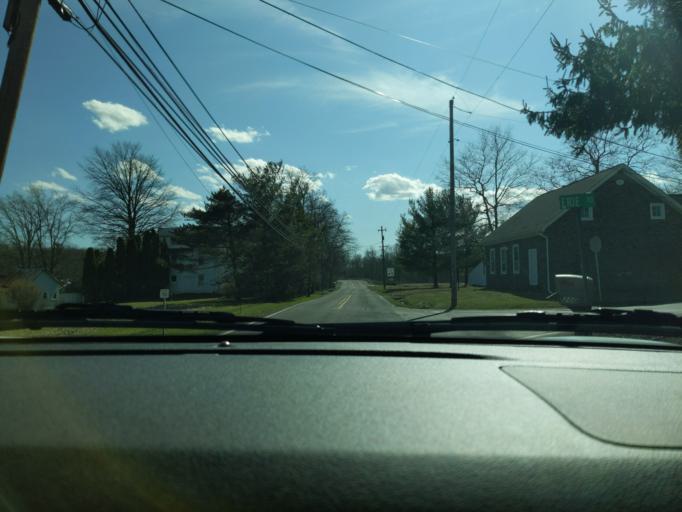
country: US
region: Pennsylvania
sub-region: Bucks County
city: Richlandtown
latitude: 40.4441
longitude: -75.3094
